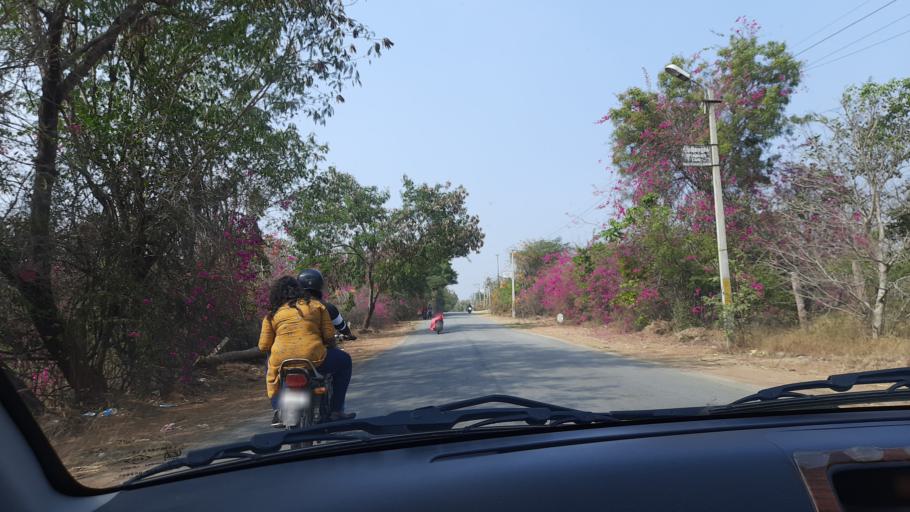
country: IN
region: Telangana
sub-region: Rangareddi
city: Lal Bahadur Nagar
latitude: 17.2779
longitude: 78.6553
